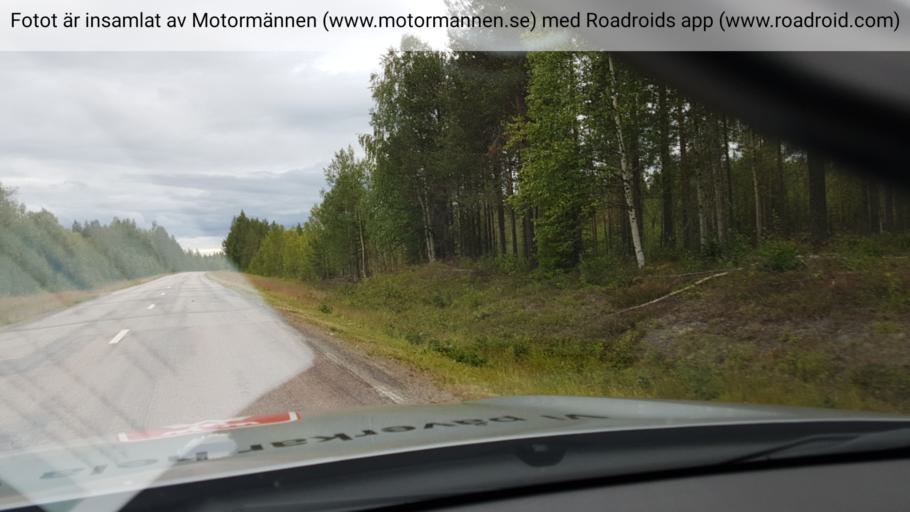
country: SE
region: Norrbotten
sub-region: Overkalix Kommun
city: OEverkalix
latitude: 66.8103
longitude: 22.9920
